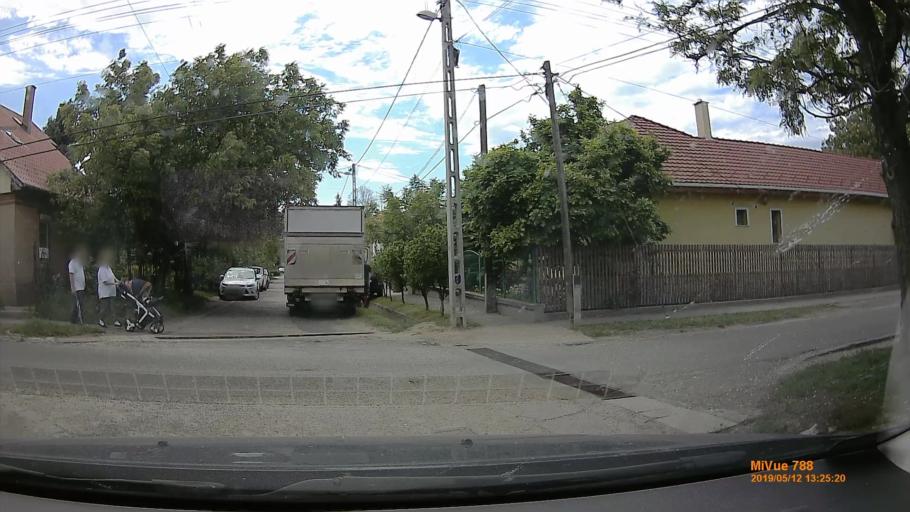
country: HU
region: Budapest
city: Budapest XVII. keruelet
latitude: 47.4851
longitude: 19.2942
